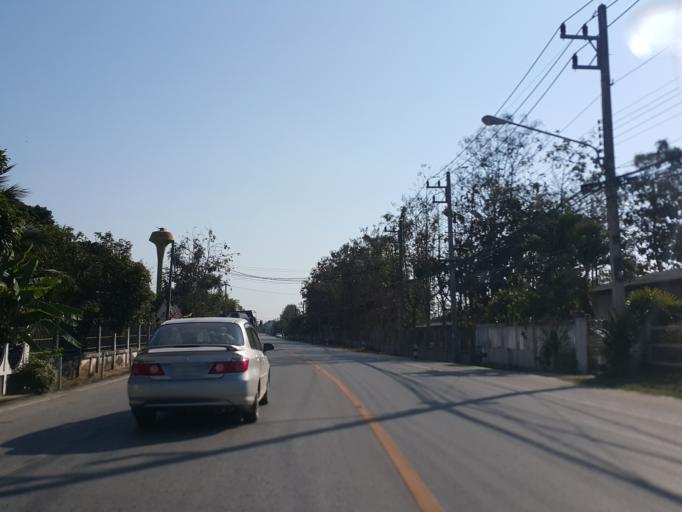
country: TH
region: Chiang Mai
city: San Sai
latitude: 18.8578
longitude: 99.1322
